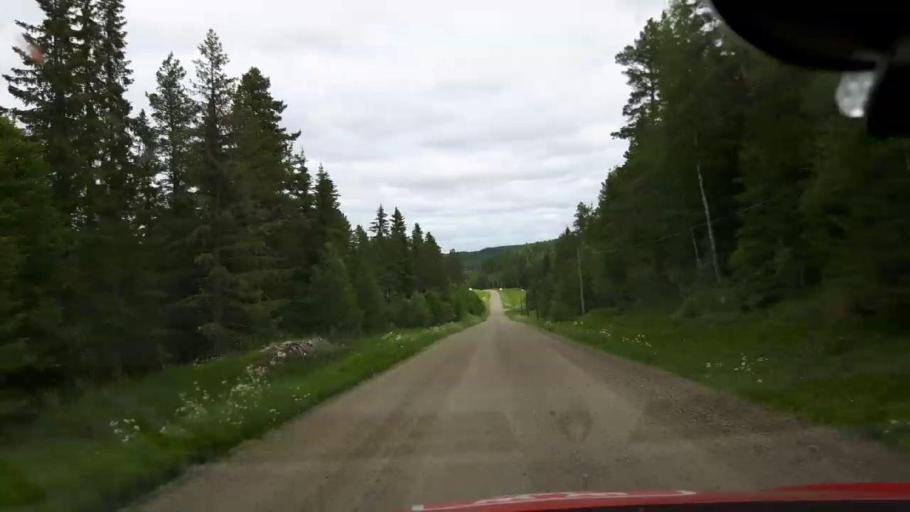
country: SE
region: Jaemtland
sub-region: OEstersunds Kommun
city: Brunflo
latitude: 62.9530
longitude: 14.9962
